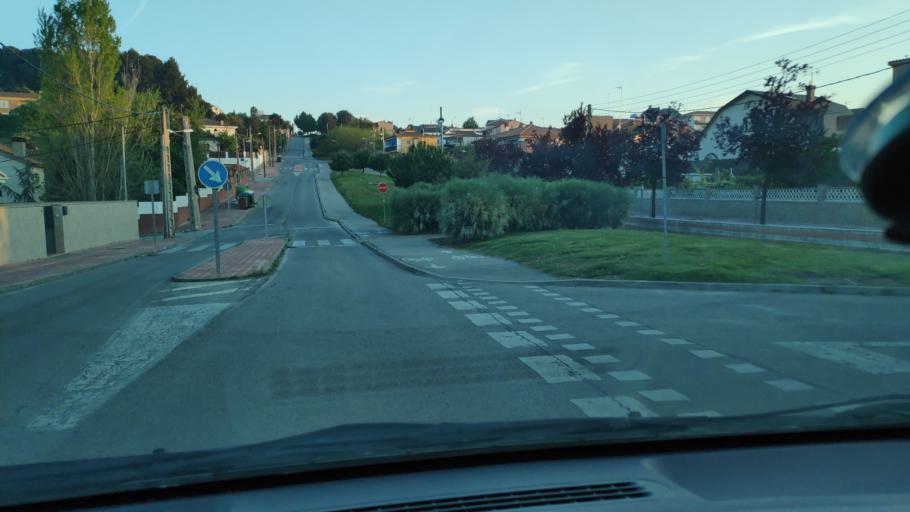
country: ES
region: Catalonia
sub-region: Provincia de Barcelona
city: Sant Quirze del Valles
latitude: 41.5362
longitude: 2.0482
